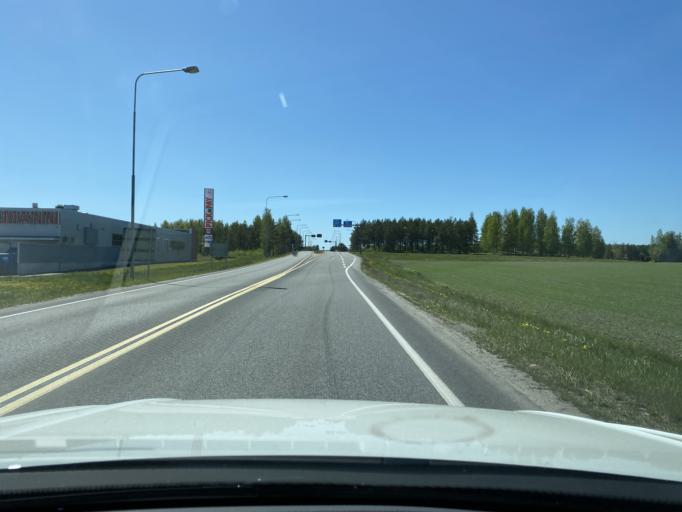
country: FI
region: Satakunta
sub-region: Pori
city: Huittinen
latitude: 61.1722
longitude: 22.6777
